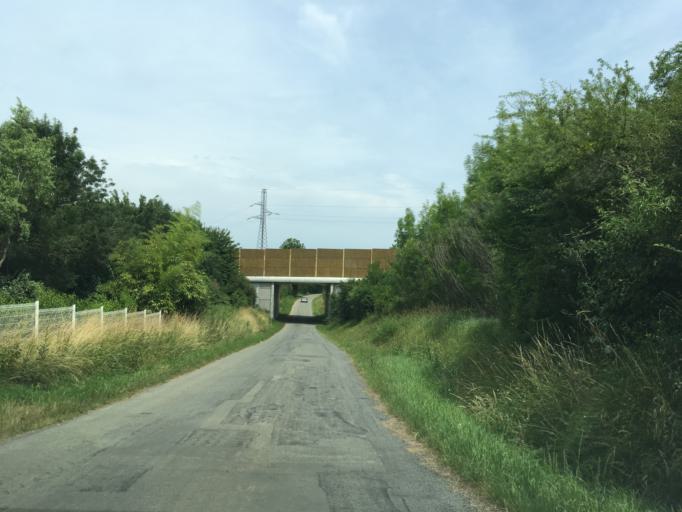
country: FR
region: Poitou-Charentes
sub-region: Departement des Deux-Sevres
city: Niort
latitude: 46.2952
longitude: -0.4700
